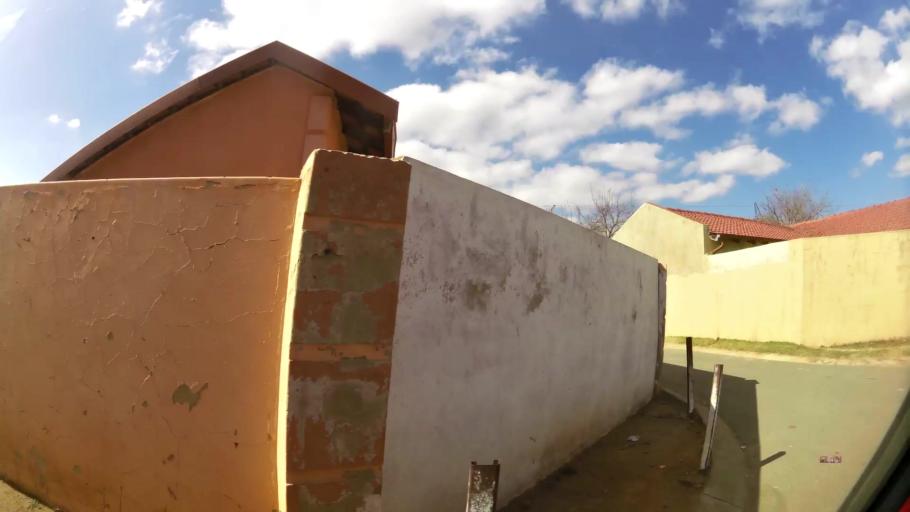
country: ZA
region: Gauteng
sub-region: City of Johannesburg Metropolitan Municipality
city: Modderfontein
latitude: -26.0307
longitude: 28.1774
